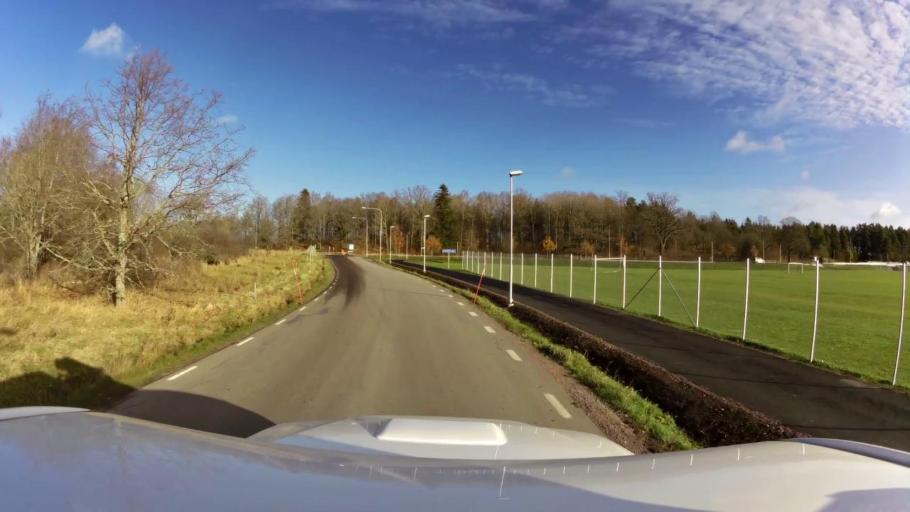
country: SE
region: OEstergoetland
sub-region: Linkopings Kommun
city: Linkoping
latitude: 58.3819
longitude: 15.6303
